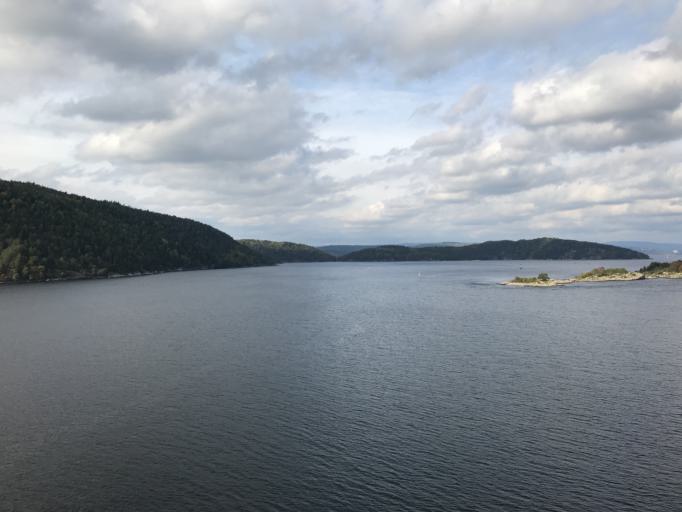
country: NO
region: Akershus
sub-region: Nesodden
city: Fagerstrand
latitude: 59.6955
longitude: 10.5979
